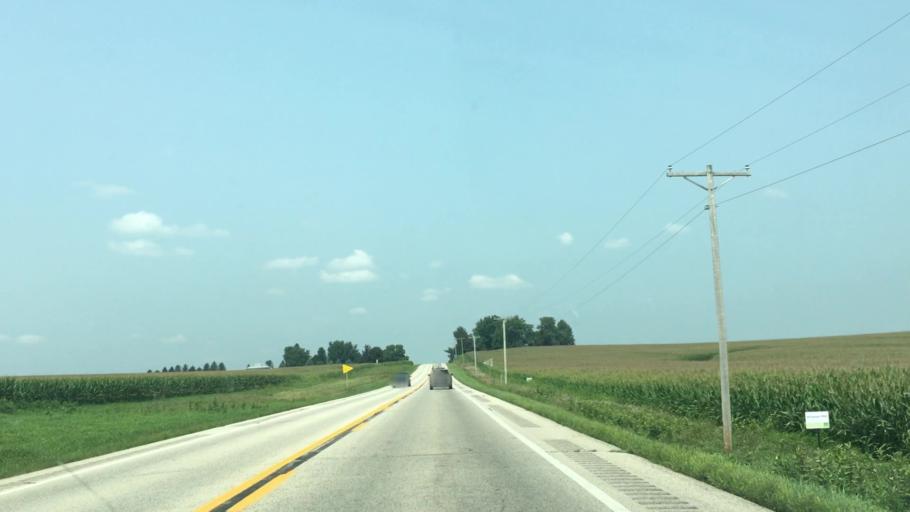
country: US
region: Iowa
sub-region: Buchanan County
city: Independence
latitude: 42.5051
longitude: -91.8896
